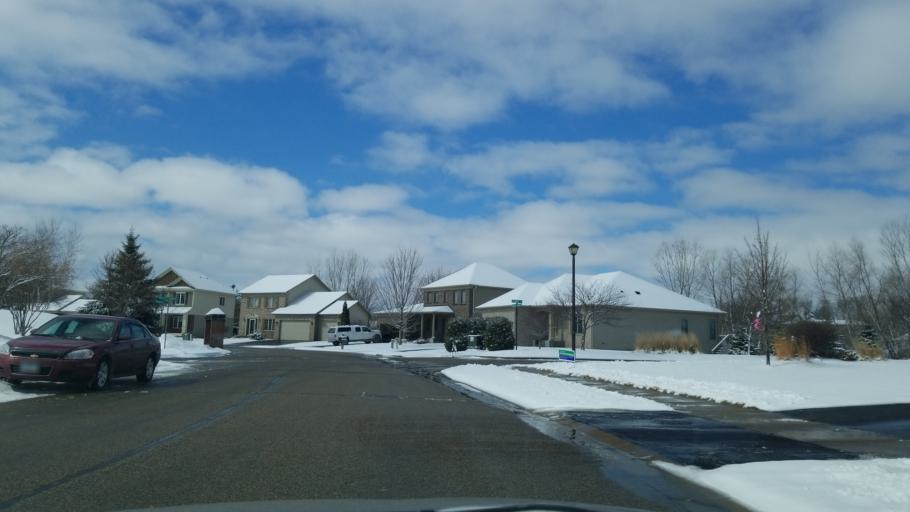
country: US
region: Wisconsin
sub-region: Saint Croix County
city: Hudson
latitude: 44.9545
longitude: -92.7090
